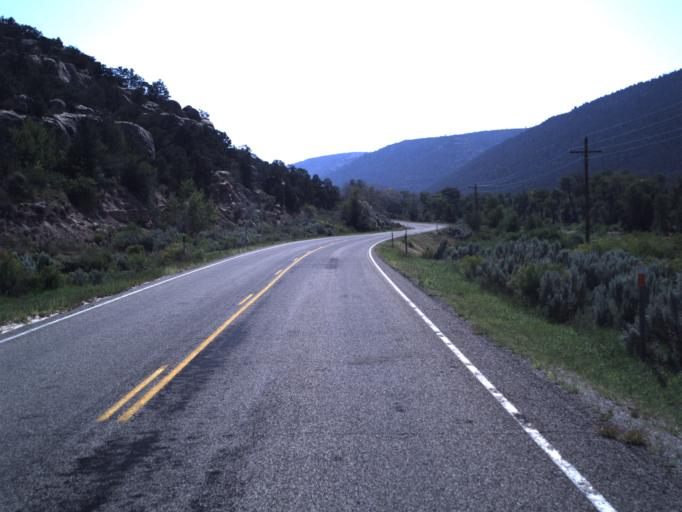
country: US
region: Utah
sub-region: Duchesne County
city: Duchesne
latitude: 40.3058
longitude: -110.6284
